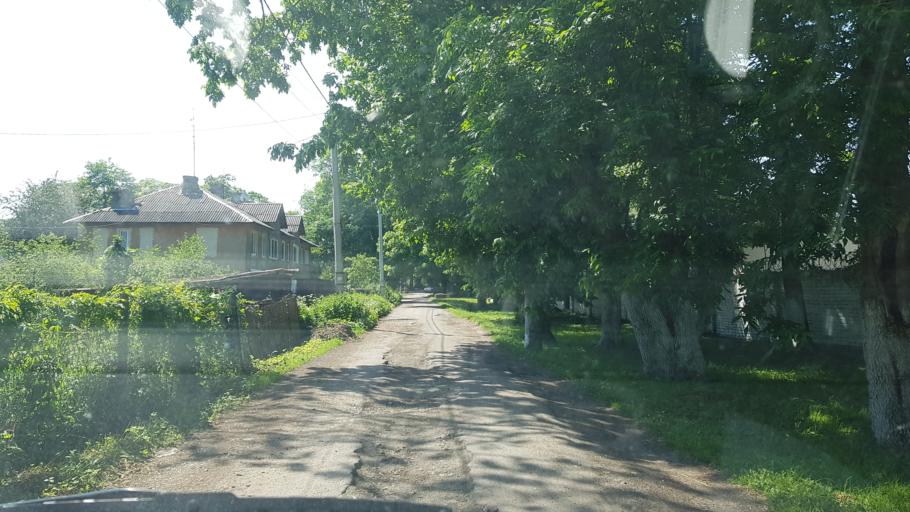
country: RU
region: Kaliningrad
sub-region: Gorod Kaliningrad
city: Baltiysk
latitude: 54.6472
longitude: 19.8880
